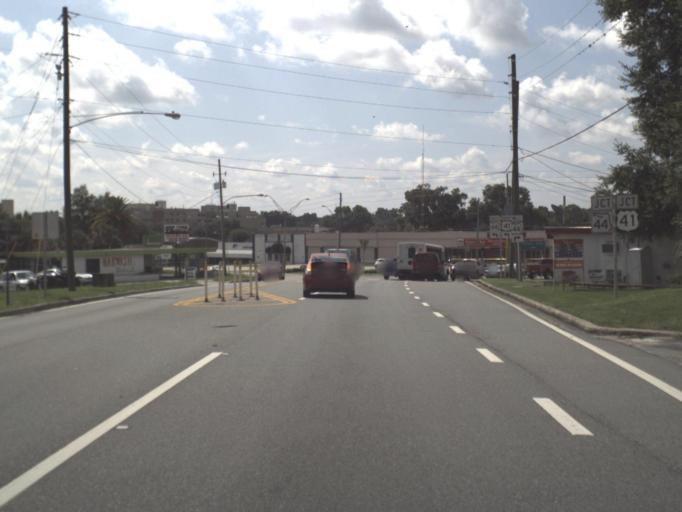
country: US
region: Florida
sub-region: Citrus County
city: Inverness
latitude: 28.8369
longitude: -82.3412
